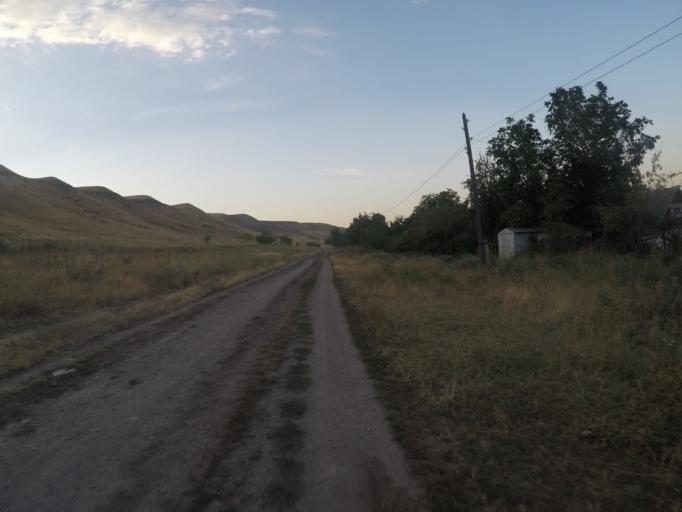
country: KG
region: Chuy
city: Bishkek
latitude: 42.7675
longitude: 74.6386
